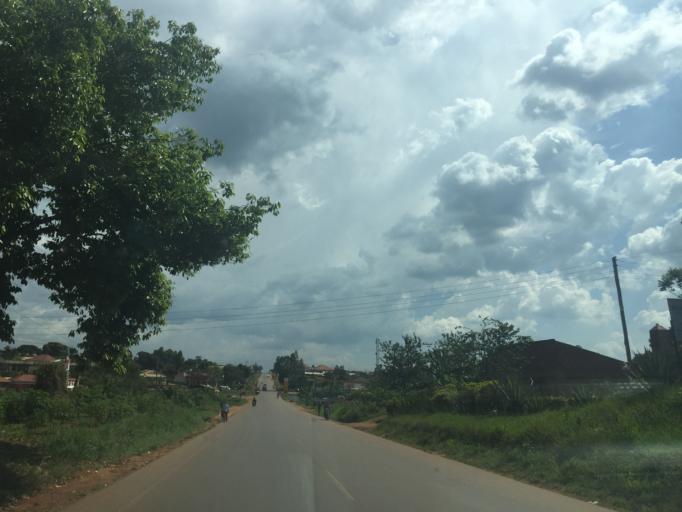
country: UG
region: Central Region
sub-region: Luwero District
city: Wobulenzi
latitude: 0.7252
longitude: 32.5282
